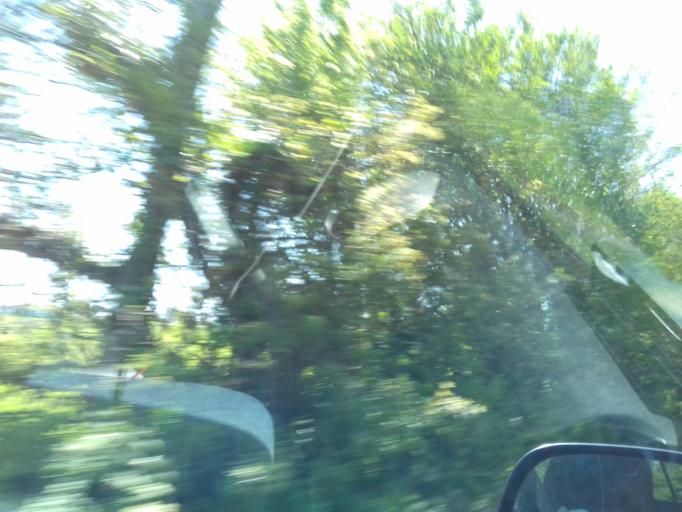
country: IE
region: Munster
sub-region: Waterford
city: Dunmore East
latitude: 52.1672
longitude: -6.8840
